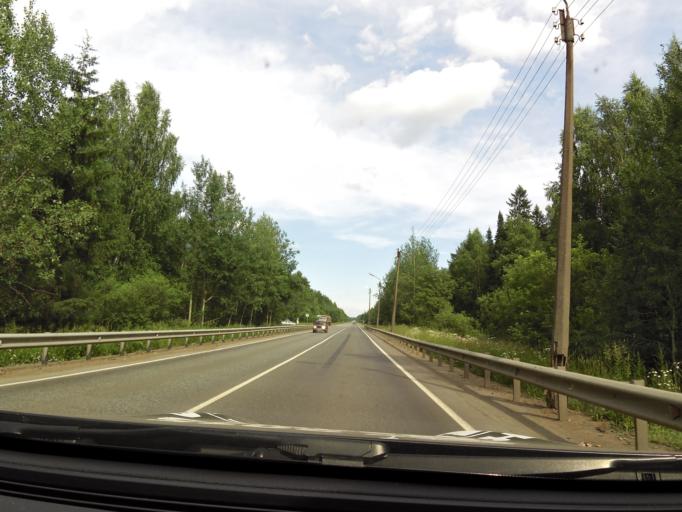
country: RU
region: Kirov
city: Slobodskoy
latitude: 58.7251
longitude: 50.2015
